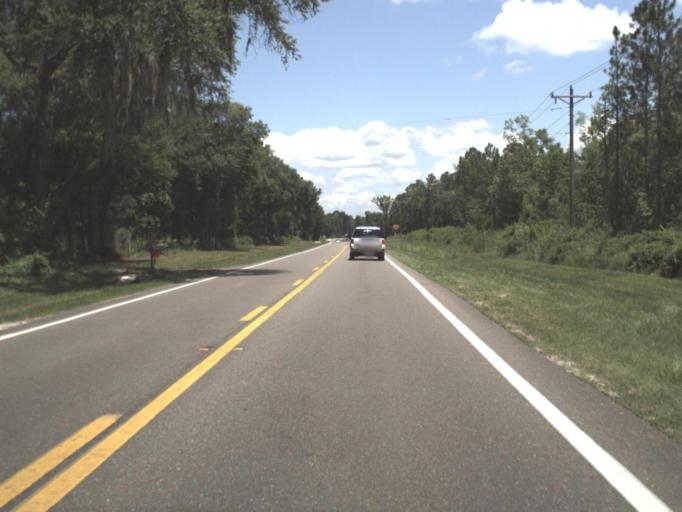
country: US
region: Florida
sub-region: Clay County
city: Keystone Heights
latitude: 29.7461
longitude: -82.0533
